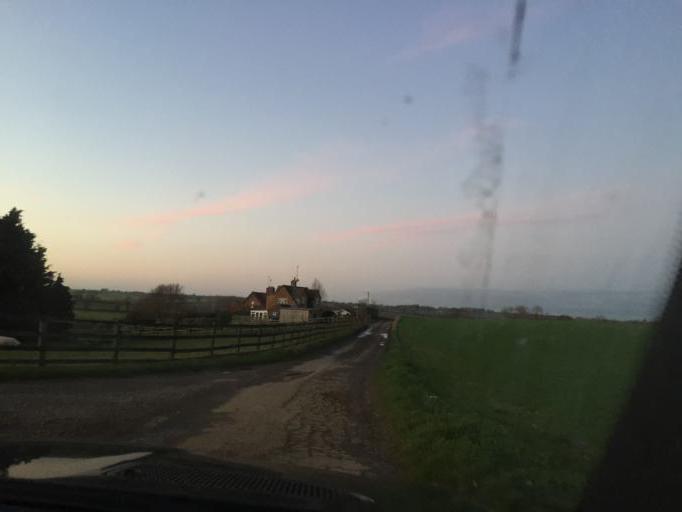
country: GB
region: England
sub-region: Northamptonshire
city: Brackley
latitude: 52.0912
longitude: -1.1116
